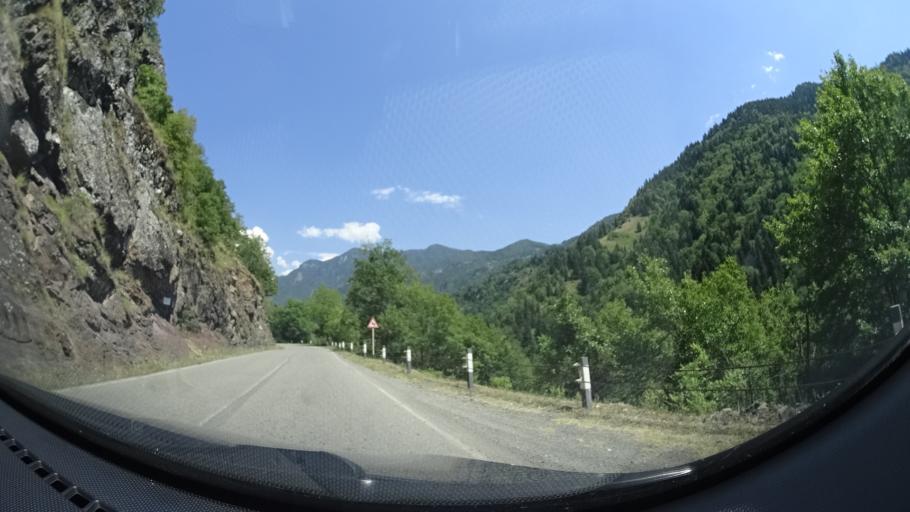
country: GE
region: Ajaria
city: Khulo
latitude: 41.6245
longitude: 42.2769
